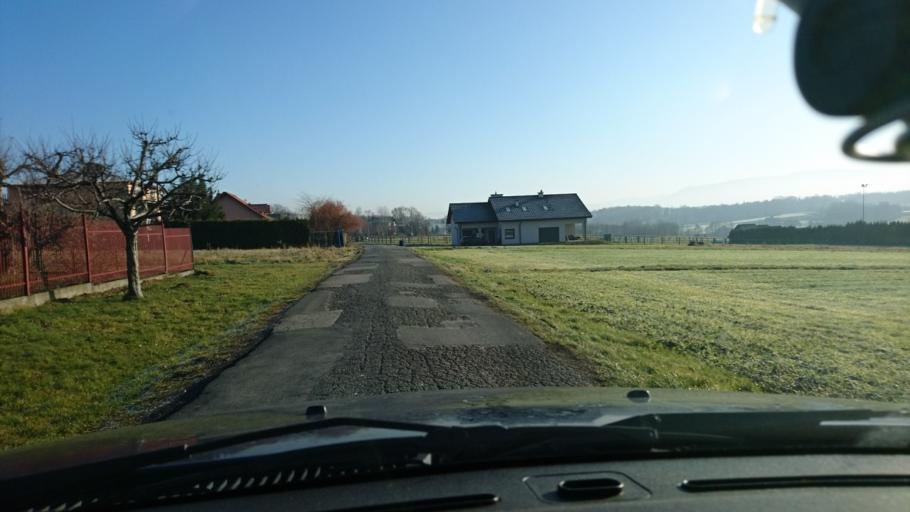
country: PL
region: Silesian Voivodeship
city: Janowice
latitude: 49.8981
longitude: 19.0956
